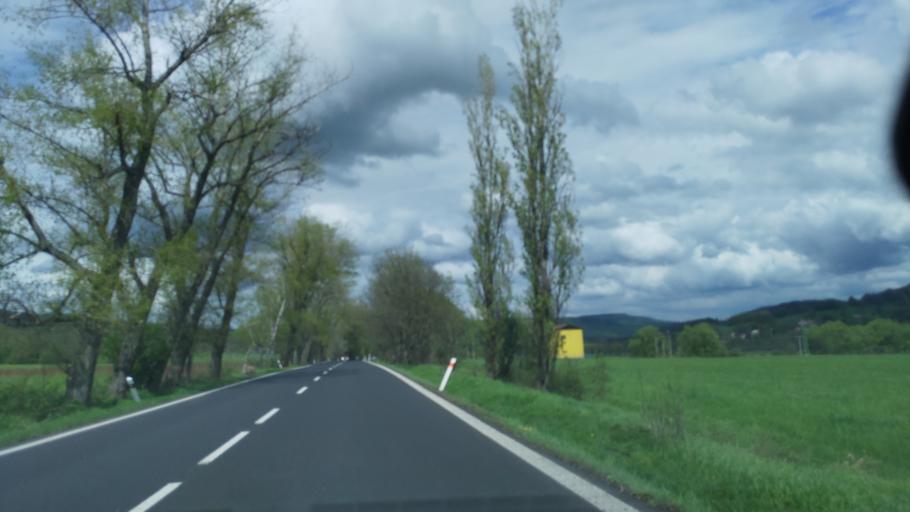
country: CZ
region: Ustecky
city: Libouchec
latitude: 50.7324
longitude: 14.0106
